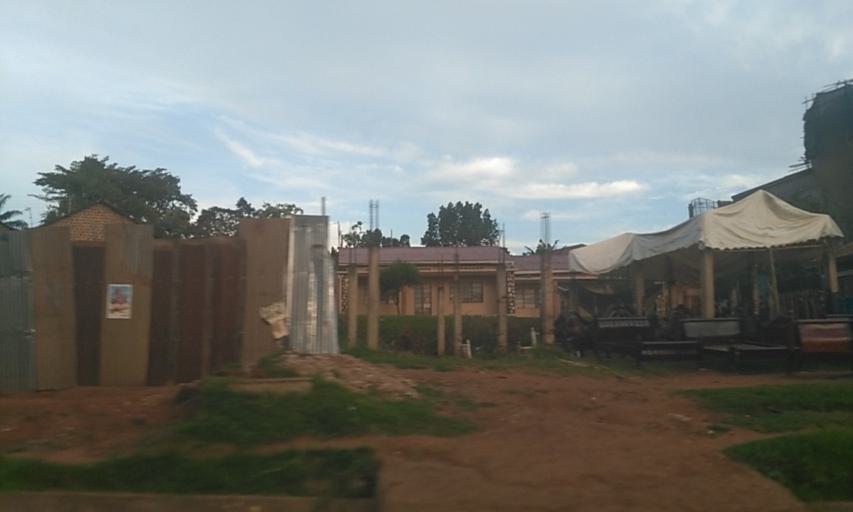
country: UG
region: Central Region
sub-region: Kampala District
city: Kampala
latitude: 0.2764
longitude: 32.5654
